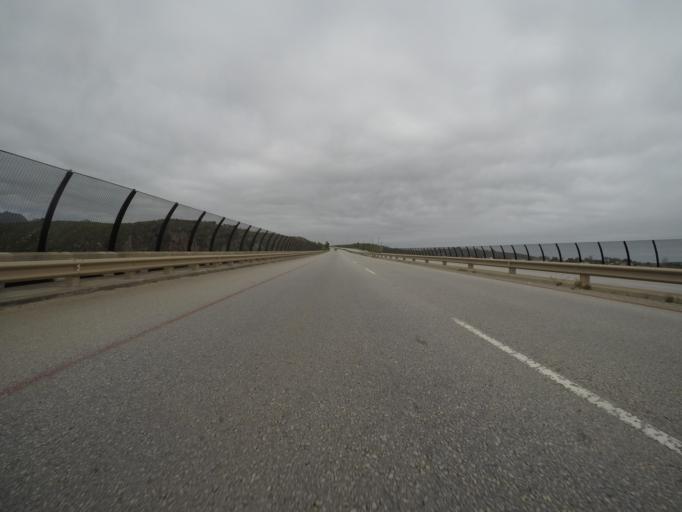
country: ZA
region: Eastern Cape
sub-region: Nelson Mandela Bay Metropolitan Municipality
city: Uitenhage
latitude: -33.9091
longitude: 25.1973
